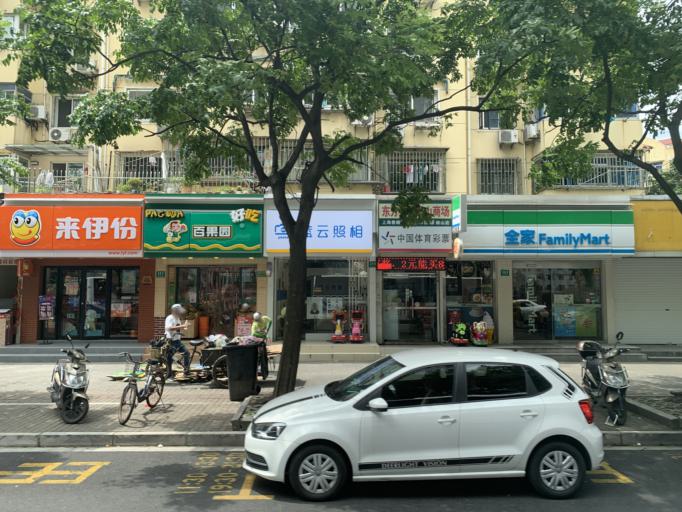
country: CN
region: Shanghai Shi
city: Huamu
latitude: 31.2478
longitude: 121.5793
